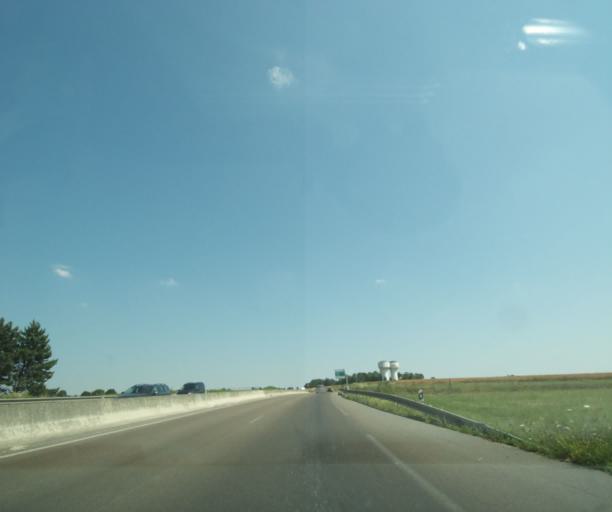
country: FR
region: Champagne-Ardenne
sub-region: Departement de la Marne
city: Saint-Memmie
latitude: 48.9579
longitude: 4.3898
